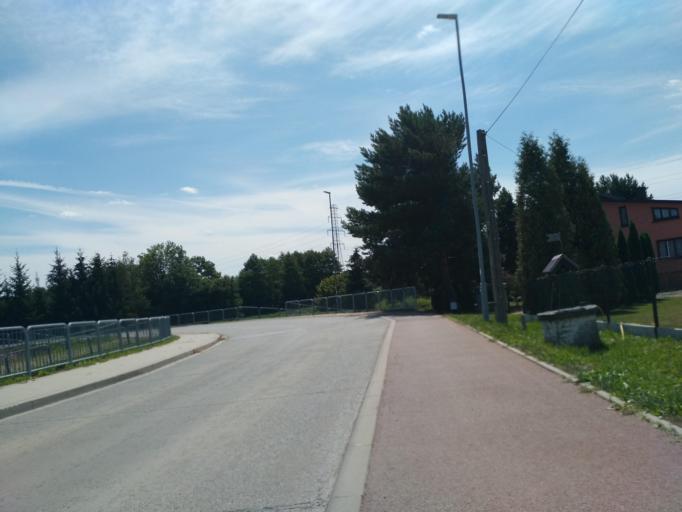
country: PL
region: Subcarpathian Voivodeship
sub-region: Powiat krosnienski
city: Korczyna
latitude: 49.6960
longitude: 21.7999
